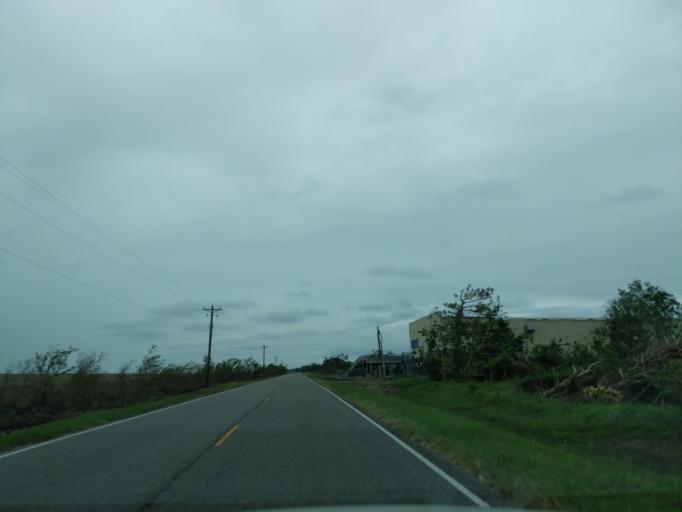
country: US
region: Louisiana
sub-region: Cameron Parish
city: Cameron
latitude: 29.7869
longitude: -93.1487
